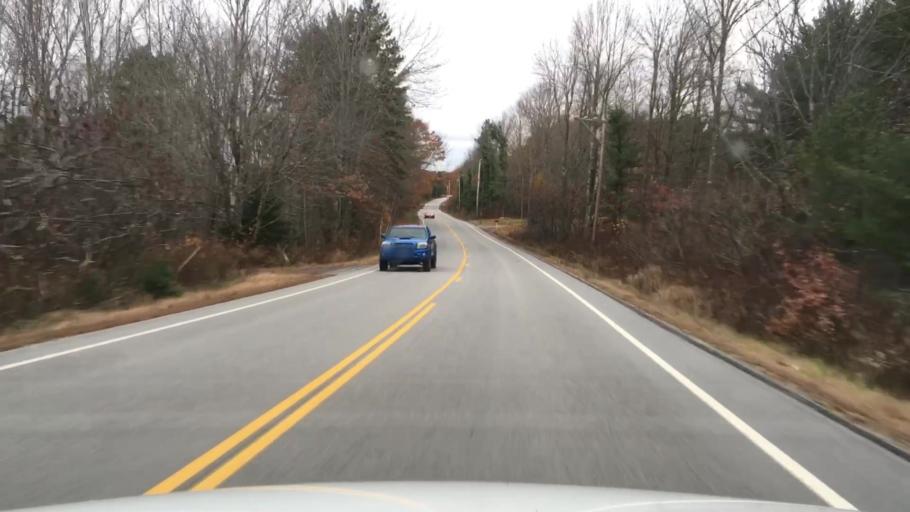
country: US
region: Maine
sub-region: Hancock County
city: Orland
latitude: 44.5382
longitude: -68.6806
